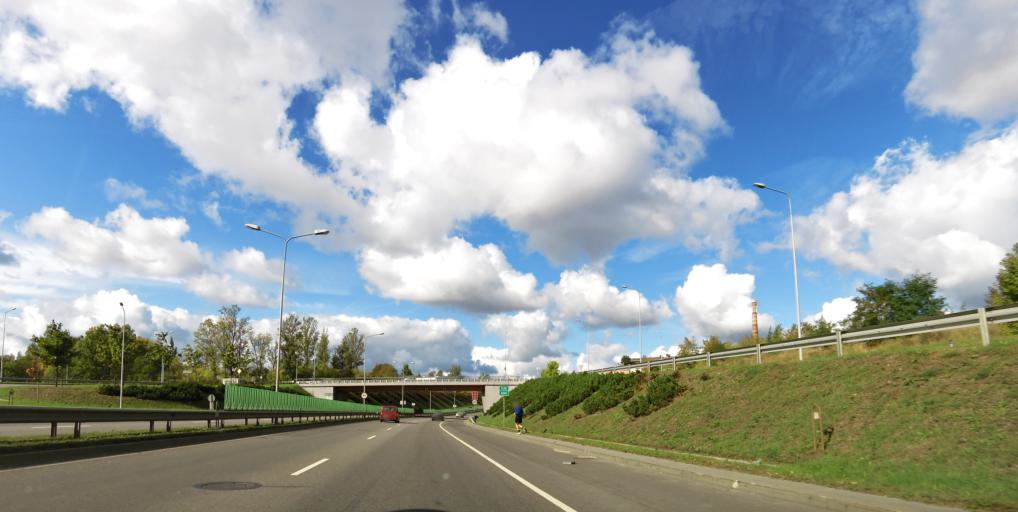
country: LT
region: Vilnius County
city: Vilkpede
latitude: 54.6616
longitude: 25.2591
